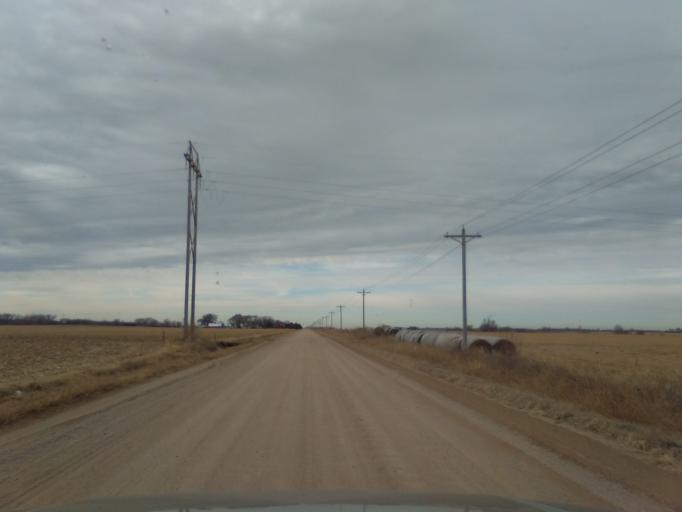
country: US
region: Nebraska
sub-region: Buffalo County
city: Gibbon
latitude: 40.6407
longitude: -98.8845
